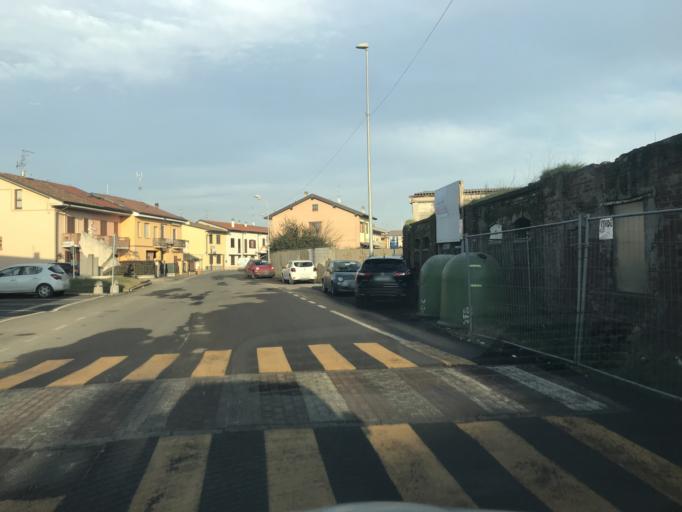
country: IT
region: Lombardy
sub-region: Provincia di Lodi
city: Borgo San Giovanni
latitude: 45.2778
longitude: 9.4362
